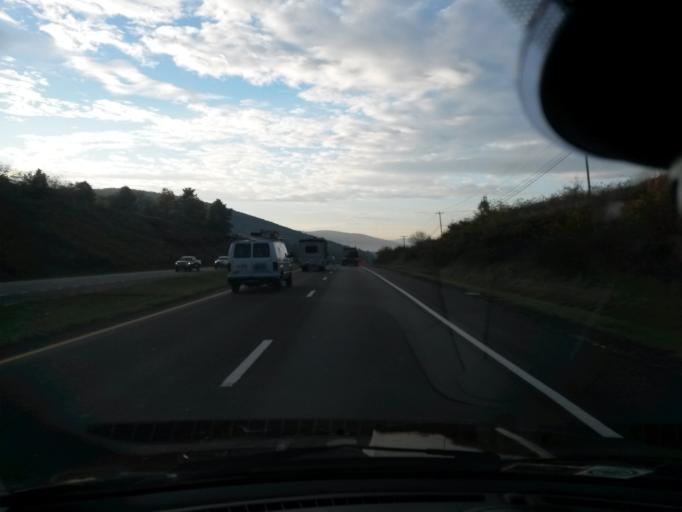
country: US
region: Virginia
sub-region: Botetourt County
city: Cloverdale
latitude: 37.3617
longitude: -79.8864
